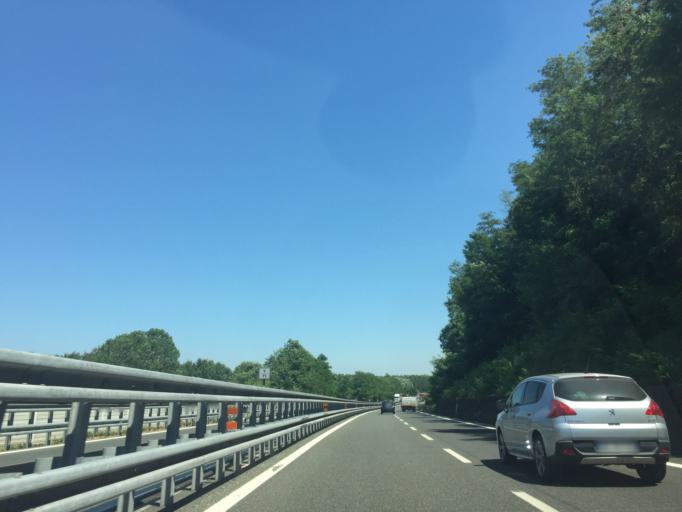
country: IT
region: Tuscany
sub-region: Provincia di Lucca
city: Lucca
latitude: 43.8529
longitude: 10.4295
